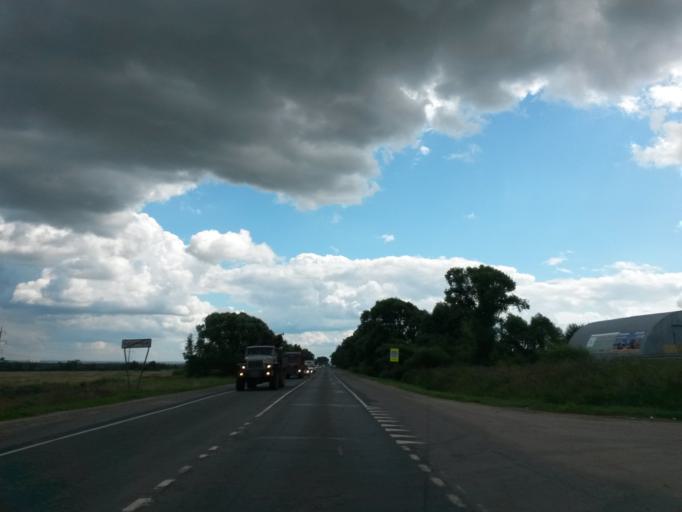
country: RU
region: Jaroslavl
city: Yaroslavl
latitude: 57.5617
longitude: 39.8419
